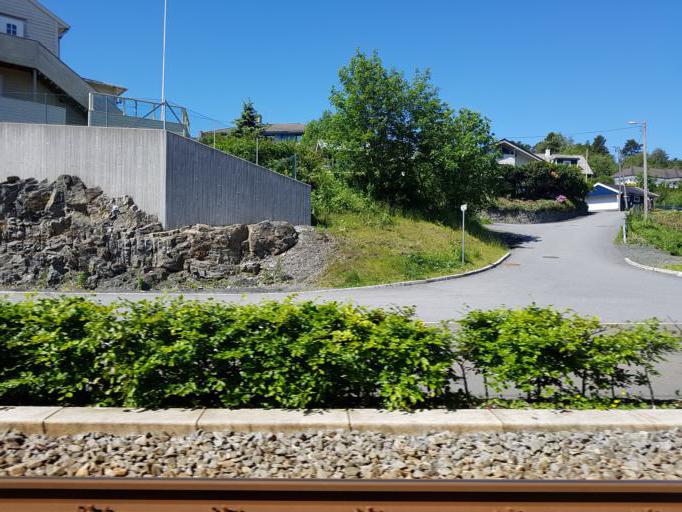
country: NO
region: Hordaland
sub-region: Bergen
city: Ytrebygda
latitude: 60.2914
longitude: 5.2658
